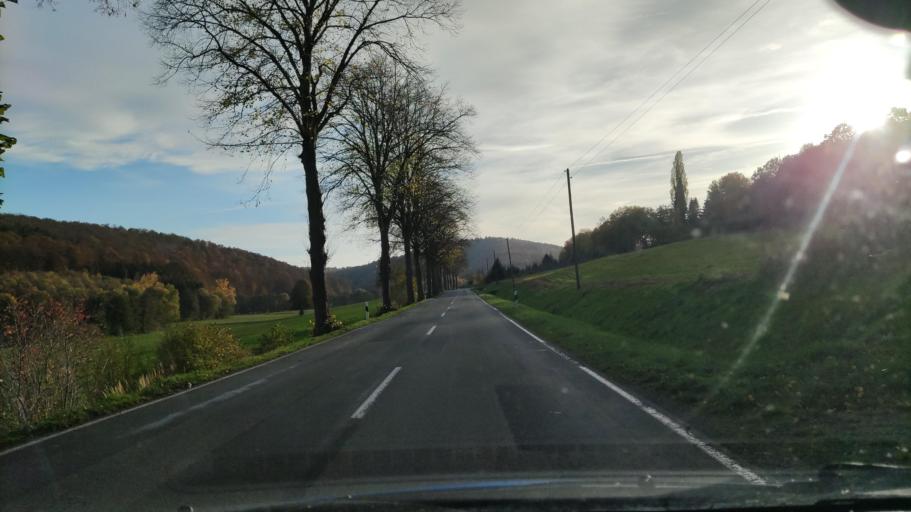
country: DE
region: Lower Saxony
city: Dassel
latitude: 51.7547
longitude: 9.7605
